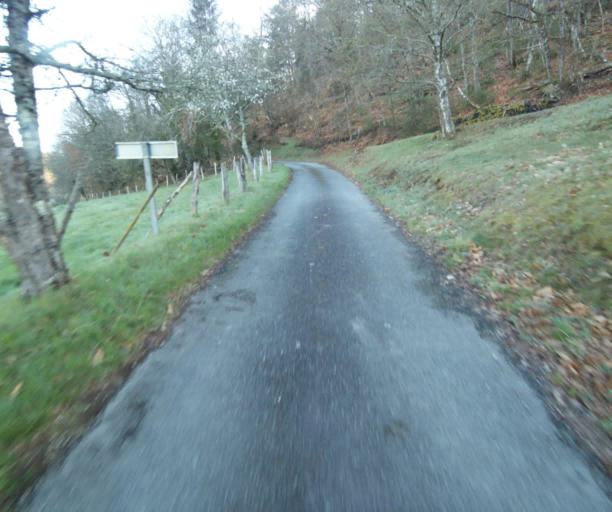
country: FR
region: Limousin
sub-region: Departement de la Correze
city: Correze
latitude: 45.3741
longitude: 1.8451
